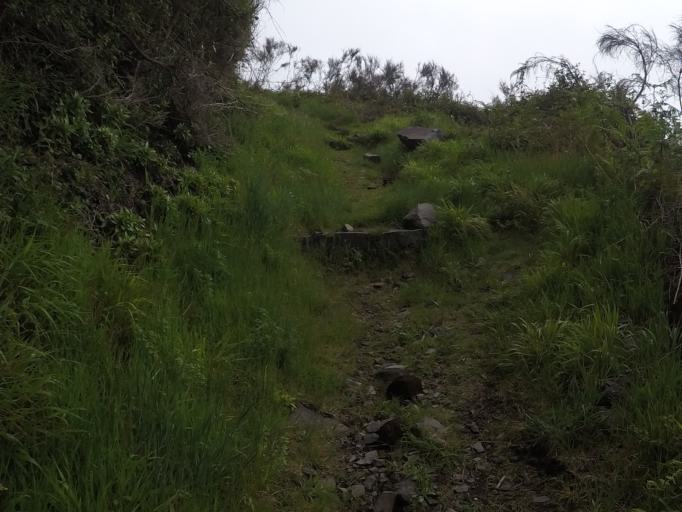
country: PT
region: Madeira
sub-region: Camara de Lobos
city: Curral das Freiras
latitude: 32.7333
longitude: -16.9899
